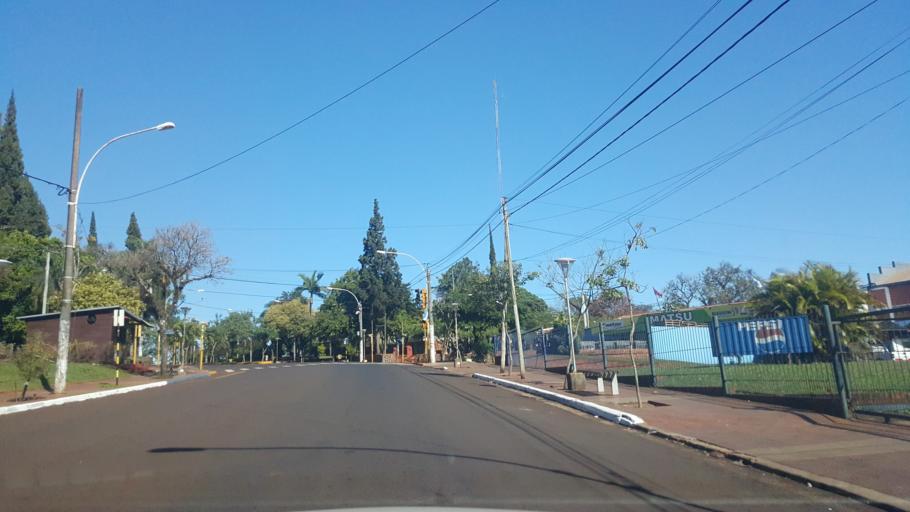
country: AR
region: Misiones
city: Puerto Rico
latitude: -26.8161
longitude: -55.0269
